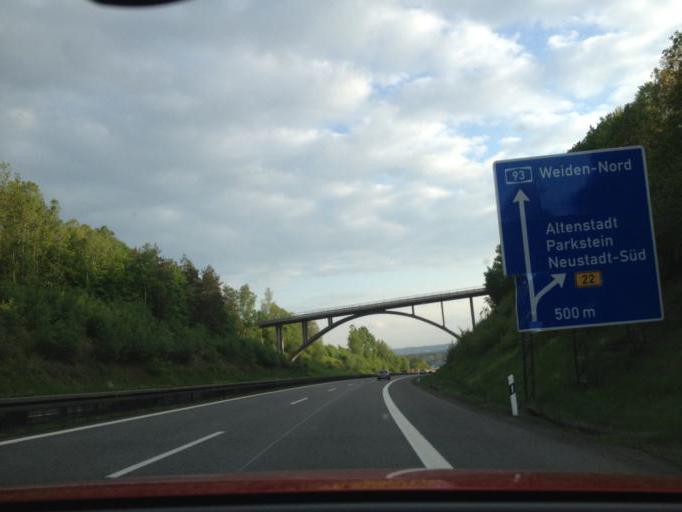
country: DE
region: Bavaria
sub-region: Upper Palatinate
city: Neustadt an der Waldnaab
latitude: 49.7290
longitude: 12.1565
